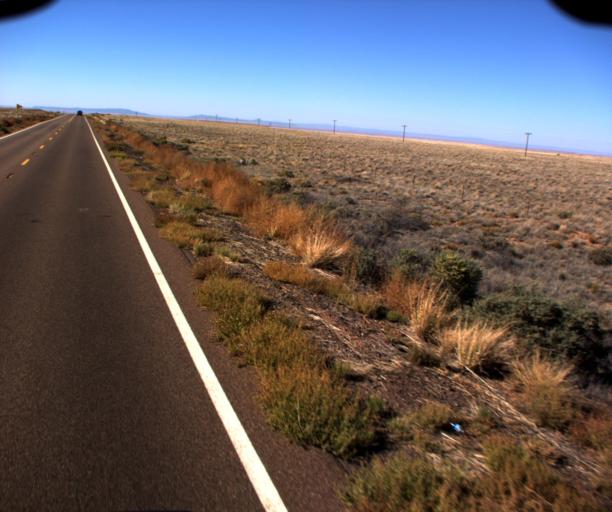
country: US
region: Arizona
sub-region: Navajo County
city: Winslow
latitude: 35.0862
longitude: -110.5524
